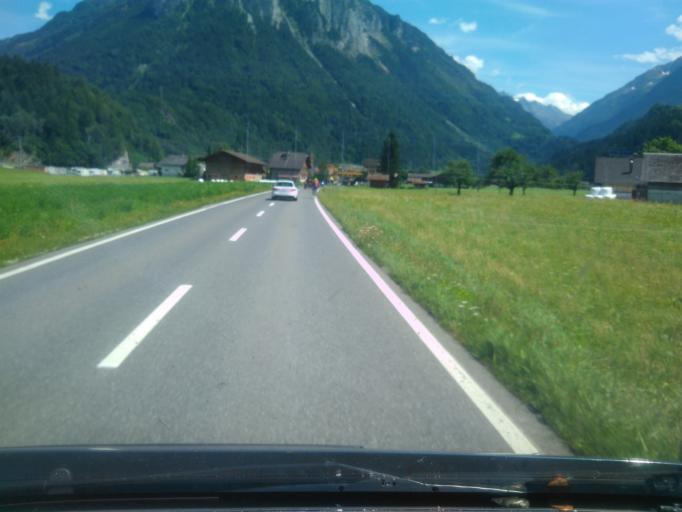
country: CH
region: Bern
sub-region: Interlaken-Oberhasli District
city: Meiringen
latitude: 46.7077
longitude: 8.2214
